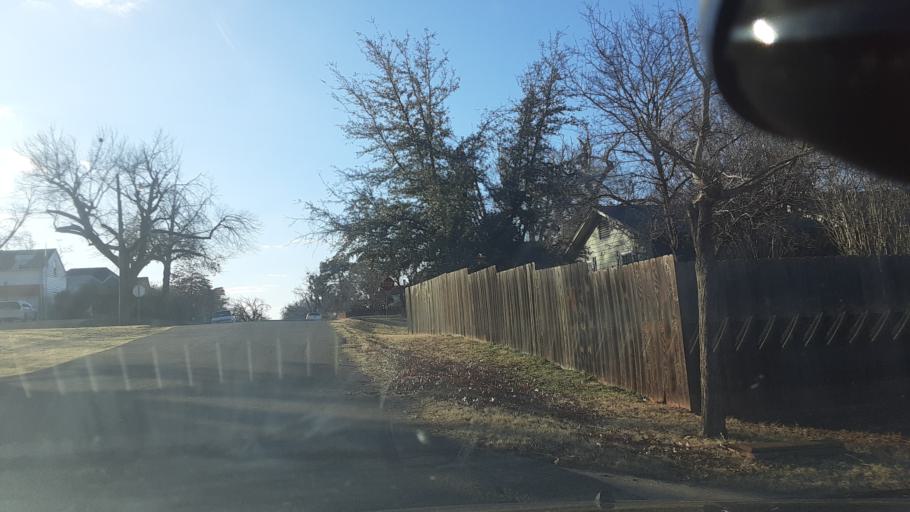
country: US
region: Oklahoma
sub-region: Logan County
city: Guthrie
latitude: 35.8823
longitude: -97.4159
